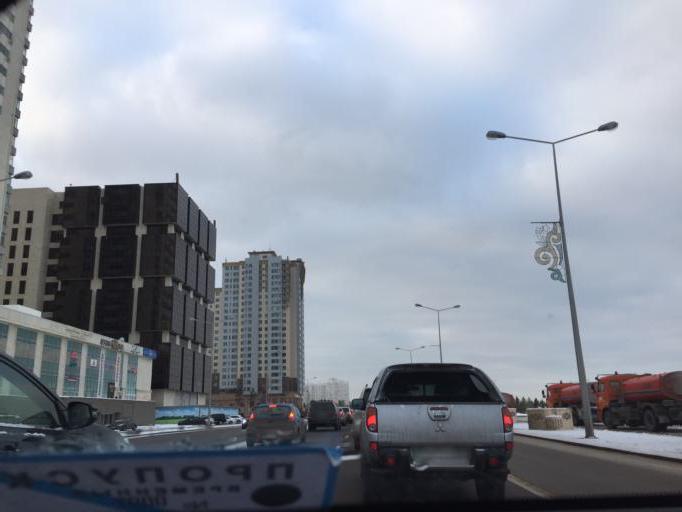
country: KZ
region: Astana Qalasy
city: Astana
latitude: 51.1317
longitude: 71.4590
